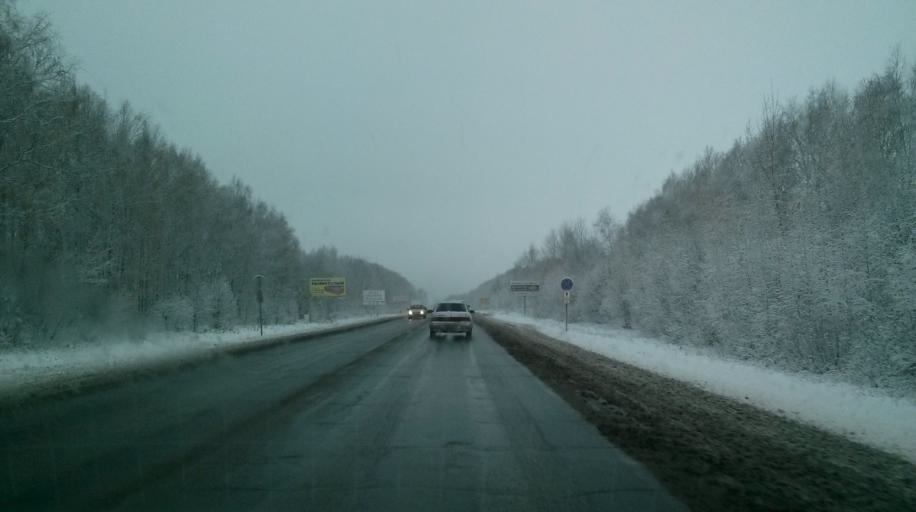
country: RU
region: Nizjnij Novgorod
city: Burevestnik
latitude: 56.1608
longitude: 43.7182
